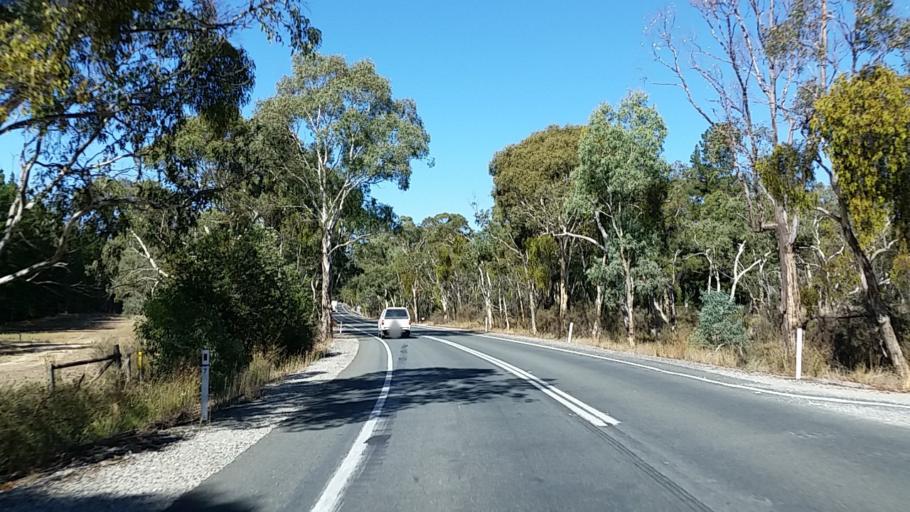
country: AU
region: South Australia
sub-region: Adelaide Hills
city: Birdwood
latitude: -34.7439
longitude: 138.9814
